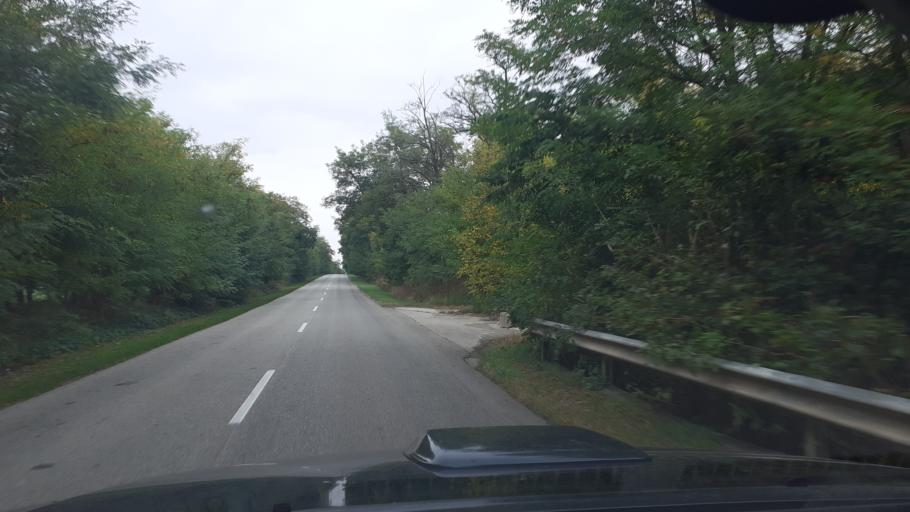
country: HU
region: Fejer
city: Baracs
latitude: 46.8461
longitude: 18.8881
